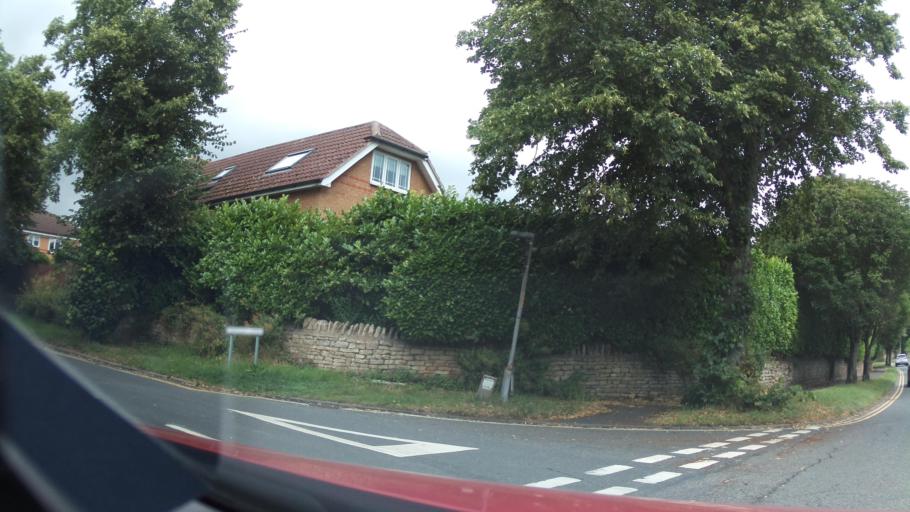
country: GB
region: England
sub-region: Lincolnshire
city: Stamford
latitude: 52.6535
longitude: -0.4699
